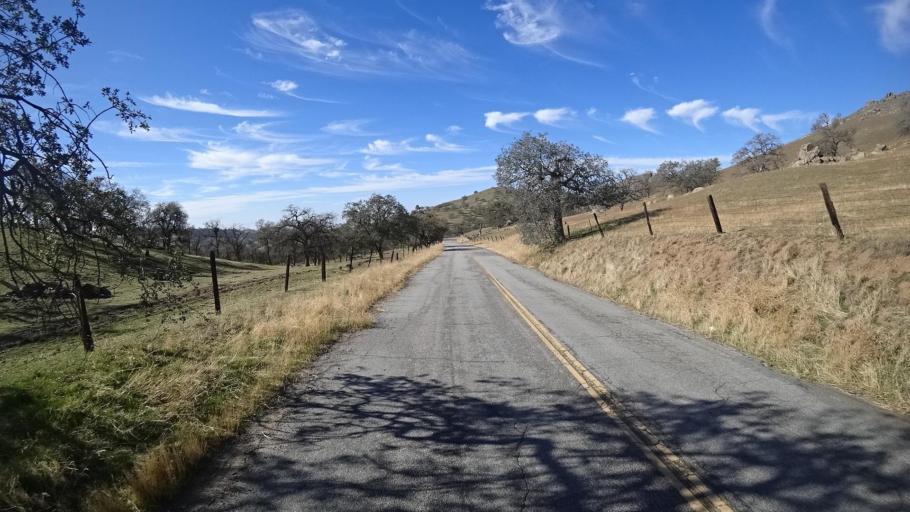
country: US
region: California
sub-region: Kern County
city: Alta Sierra
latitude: 35.6298
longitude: -118.7958
